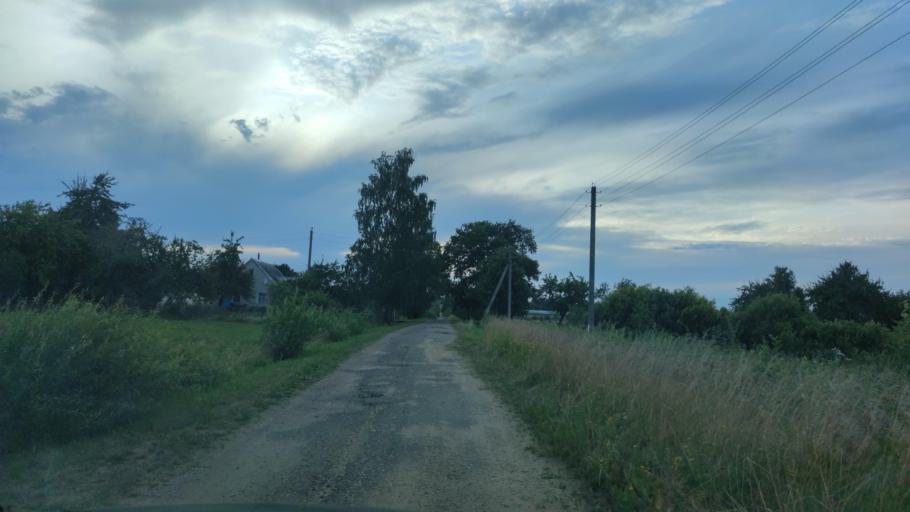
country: BY
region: Vitebsk
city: Mosar
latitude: 55.1254
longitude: 27.1693
